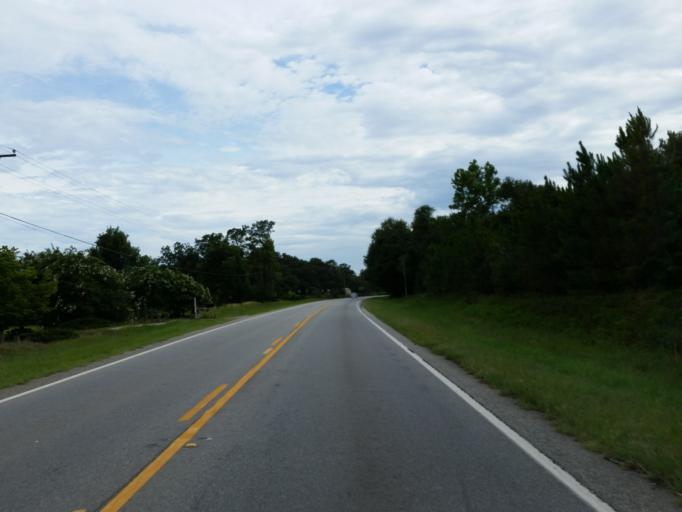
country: US
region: Georgia
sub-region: Lowndes County
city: Valdosta
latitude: 30.7335
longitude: -83.2824
